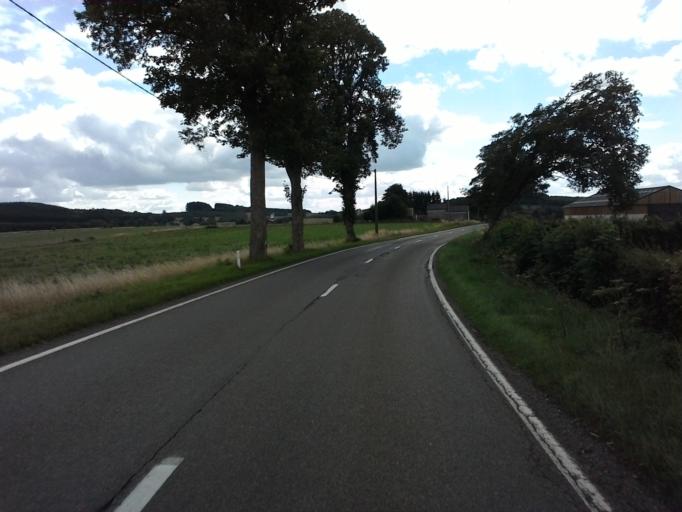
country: BE
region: Wallonia
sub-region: Province du Luxembourg
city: Leglise
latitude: 49.8065
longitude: 5.5264
